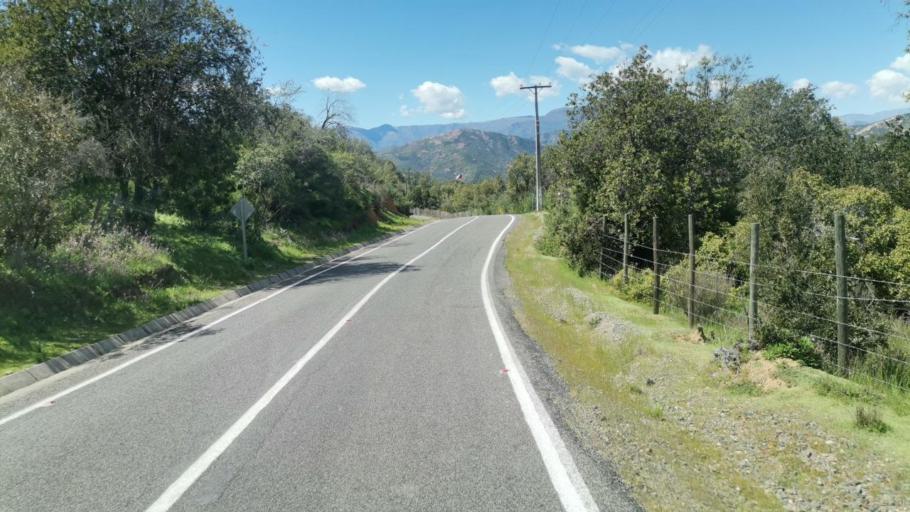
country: CL
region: Valparaiso
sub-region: Provincia de Marga Marga
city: Limache
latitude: -33.1949
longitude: -71.2112
